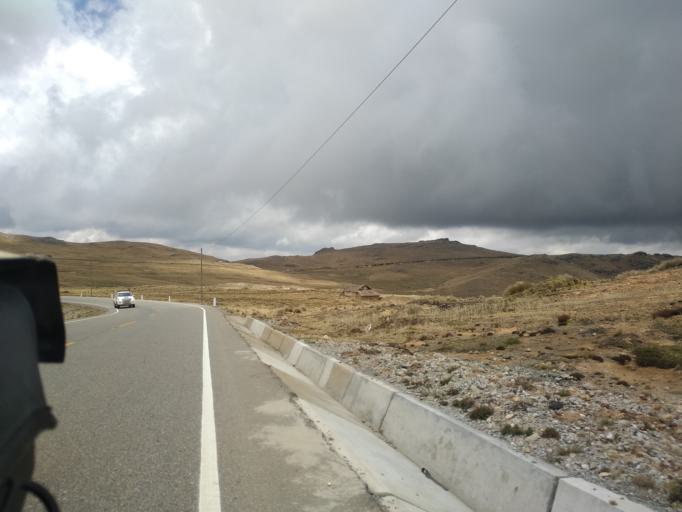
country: PE
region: La Libertad
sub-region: Provincia de Santiago de Chuco
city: Quiruvilca
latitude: -7.9436
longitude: -78.1891
